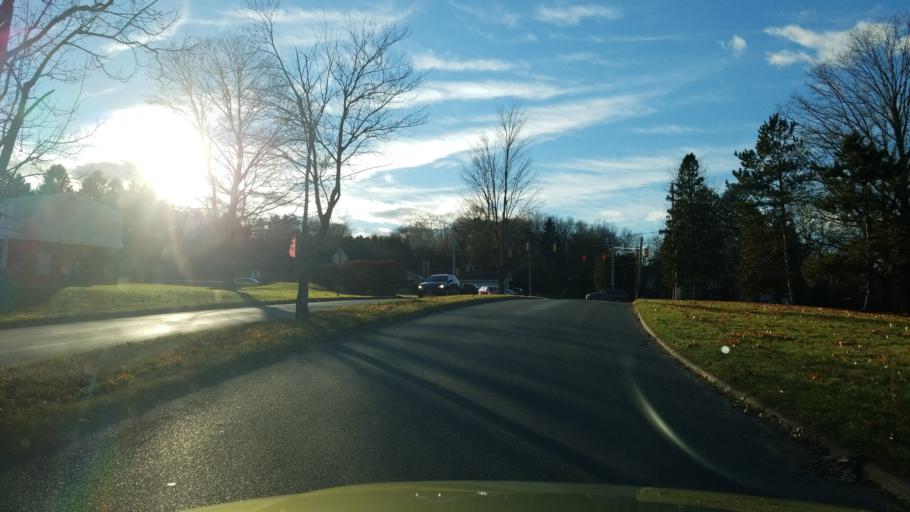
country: US
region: Pennsylvania
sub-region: Indiana County
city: Indiana
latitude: 40.6167
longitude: -79.1919
